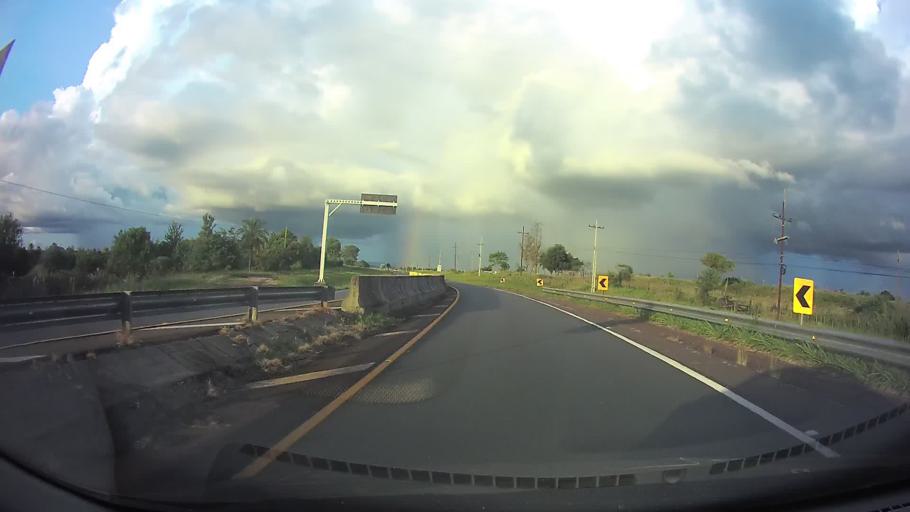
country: PY
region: Paraguari
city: Carapegua
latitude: -25.7485
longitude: -57.2158
